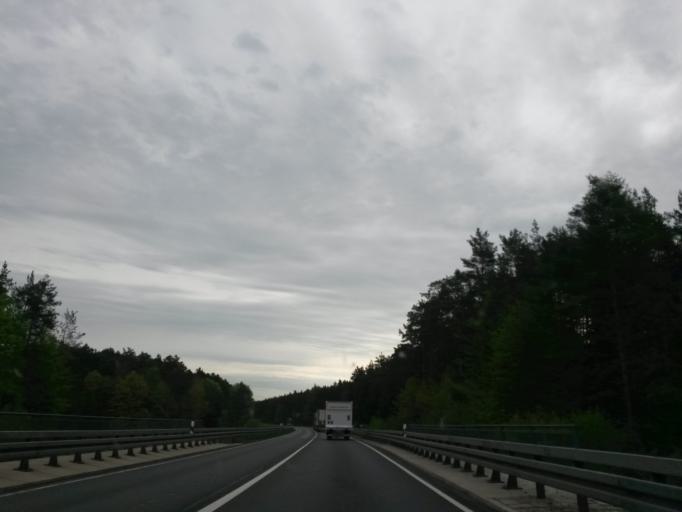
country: DE
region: Bavaria
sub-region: Upper Franconia
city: Pommersfelden
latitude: 49.7566
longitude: 10.8647
